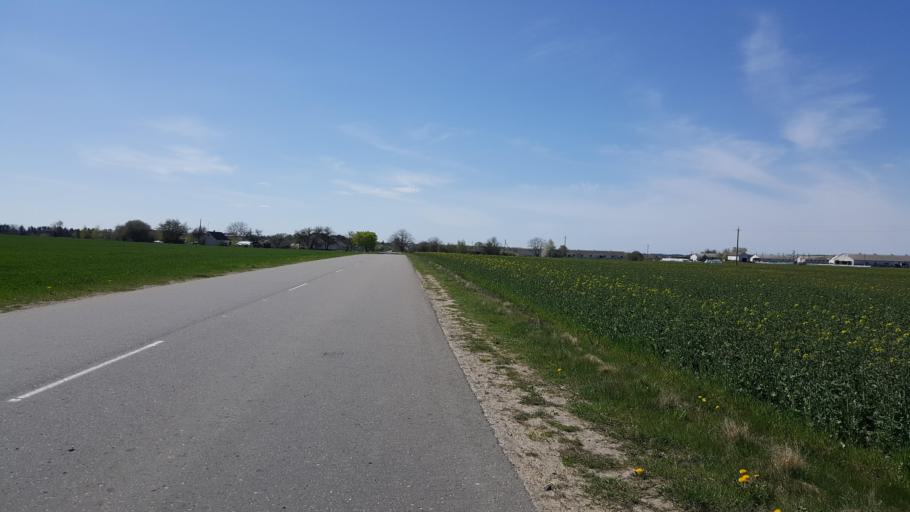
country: BY
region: Brest
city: Vysokaye
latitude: 52.3519
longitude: 23.4704
